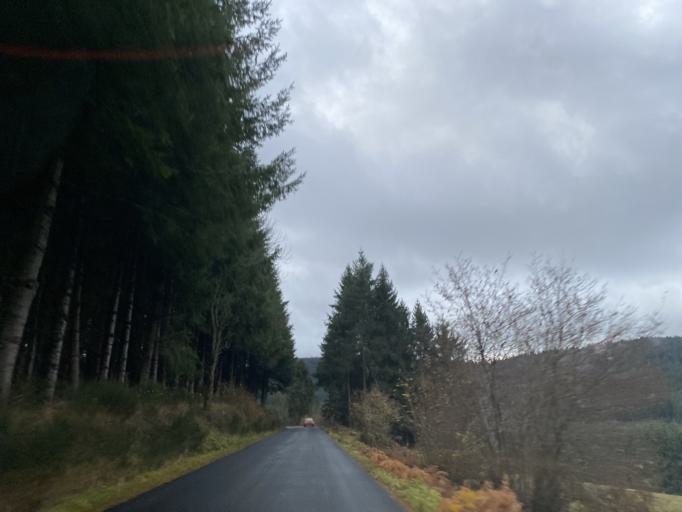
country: FR
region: Auvergne
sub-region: Departement du Puy-de-Dome
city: Cunlhat
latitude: 45.5786
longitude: 3.5597
